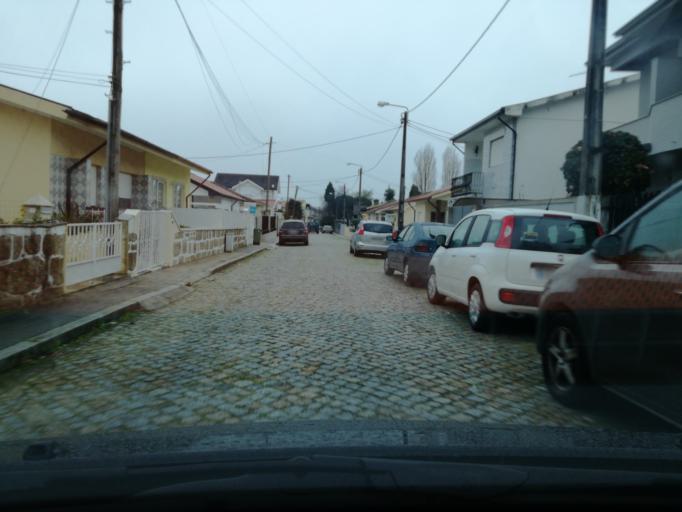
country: PT
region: Porto
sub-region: Maia
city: Gemunde
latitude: 41.2590
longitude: -8.6627
